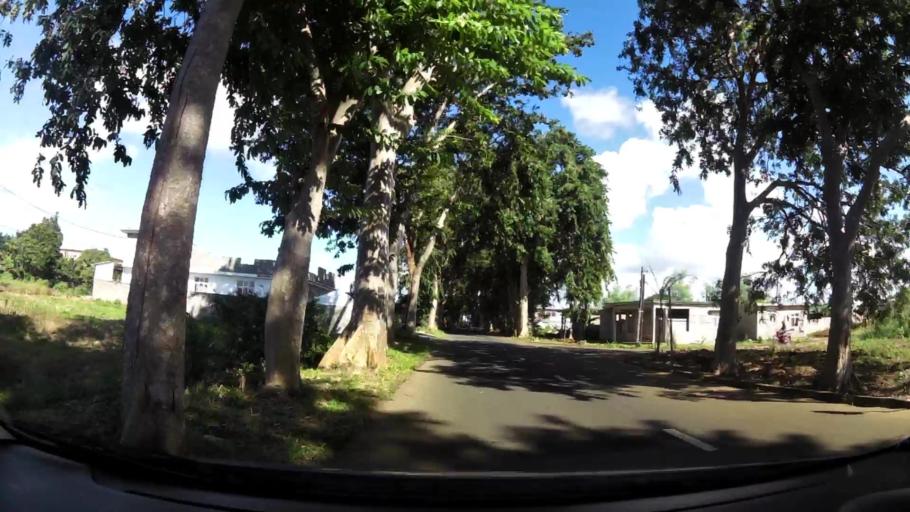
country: MU
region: Grand Port
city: Mahebourg
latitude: -20.4084
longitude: 57.6971
